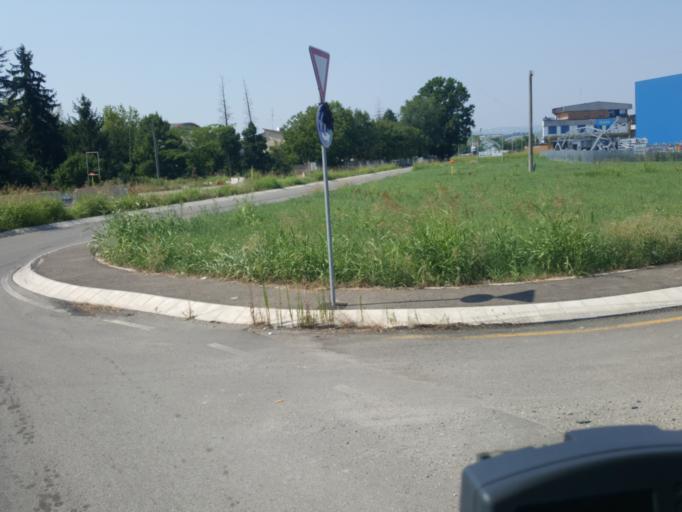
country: IT
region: Emilia-Romagna
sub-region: Provincia di Modena
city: San Vito
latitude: 44.5319
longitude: 10.9826
